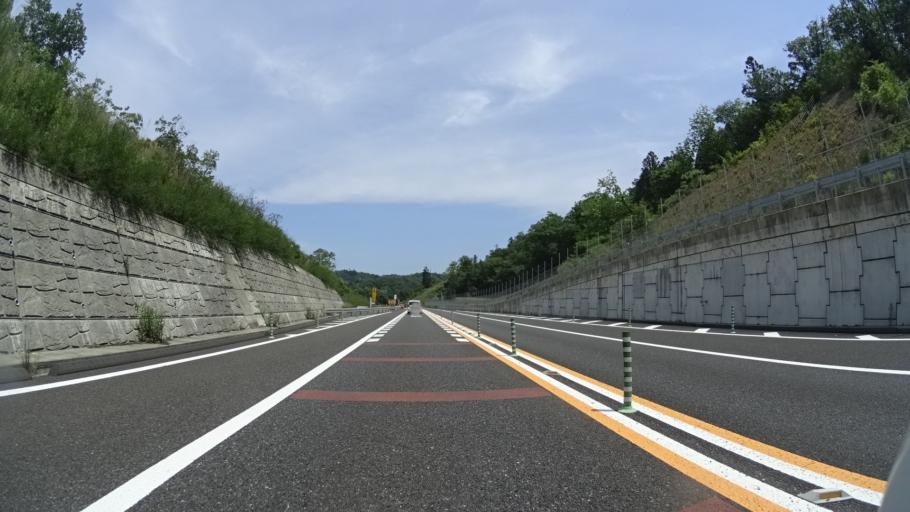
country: JP
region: Kyoto
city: Miyazu
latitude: 35.5718
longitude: 135.1213
